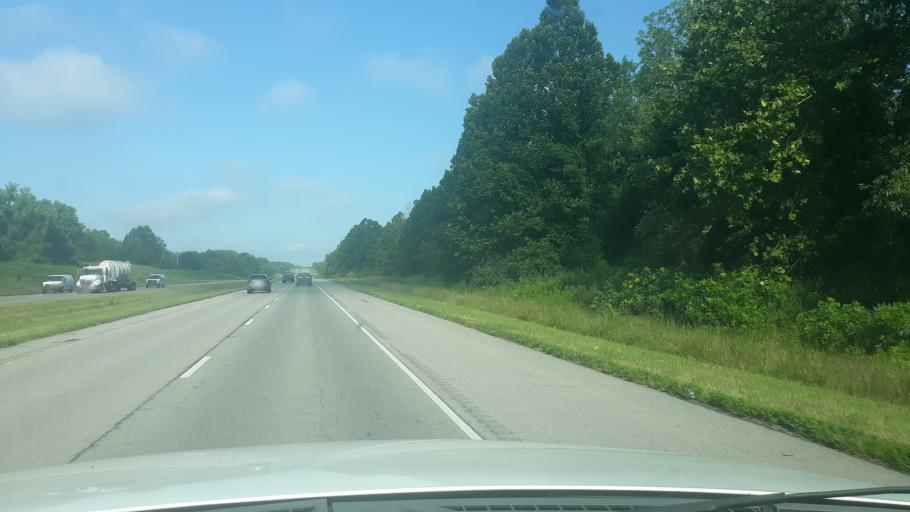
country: US
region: Illinois
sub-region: Saline County
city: Carrier Mills
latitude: 37.7308
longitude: -88.7428
